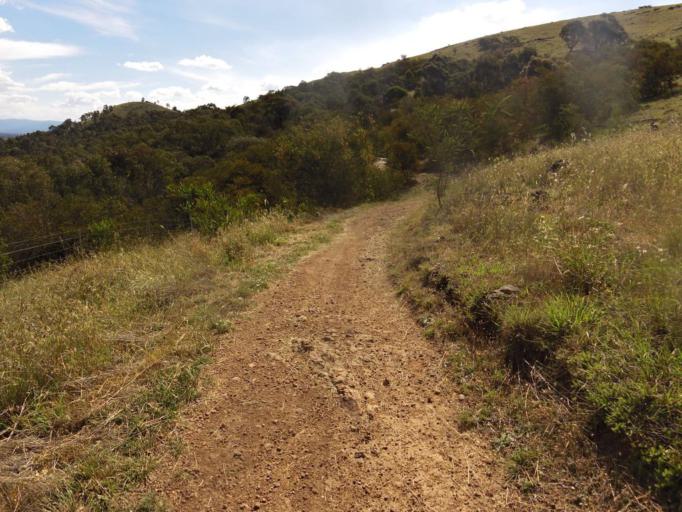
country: AU
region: Australian Capital Territory
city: Belconnen
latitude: -35.1572
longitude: 149.0802
